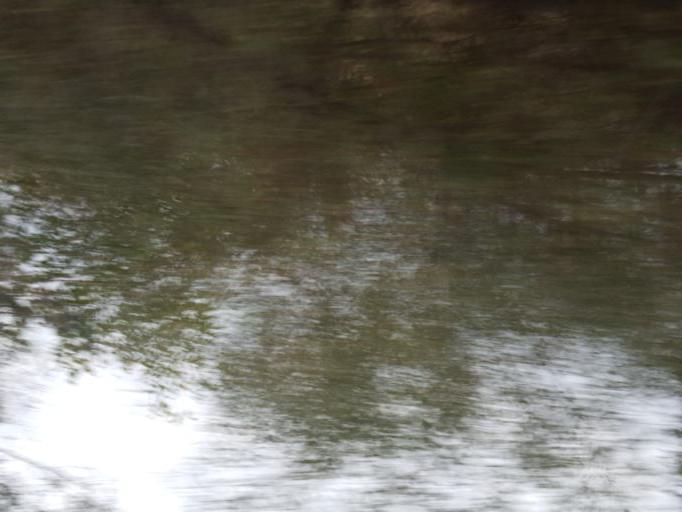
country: TR
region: Corum
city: Cemilbey
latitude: 40.2845
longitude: 35.0645
